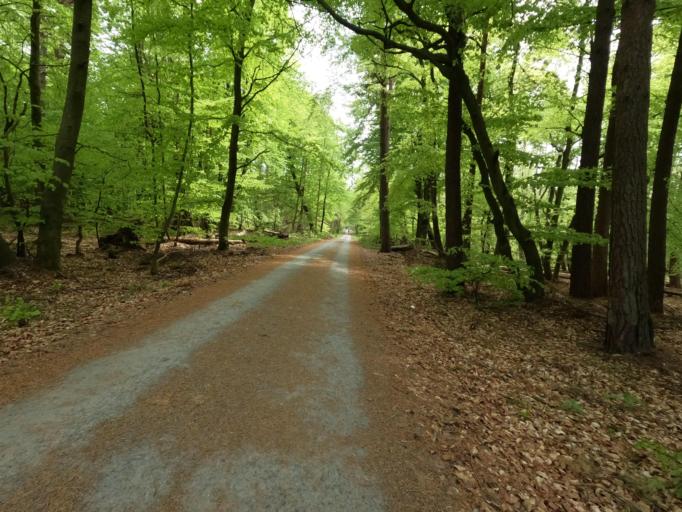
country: DE
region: Mecklenburg-Vorpommern
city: Ostseebad Prerow
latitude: 54.4629
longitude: 12.5150
